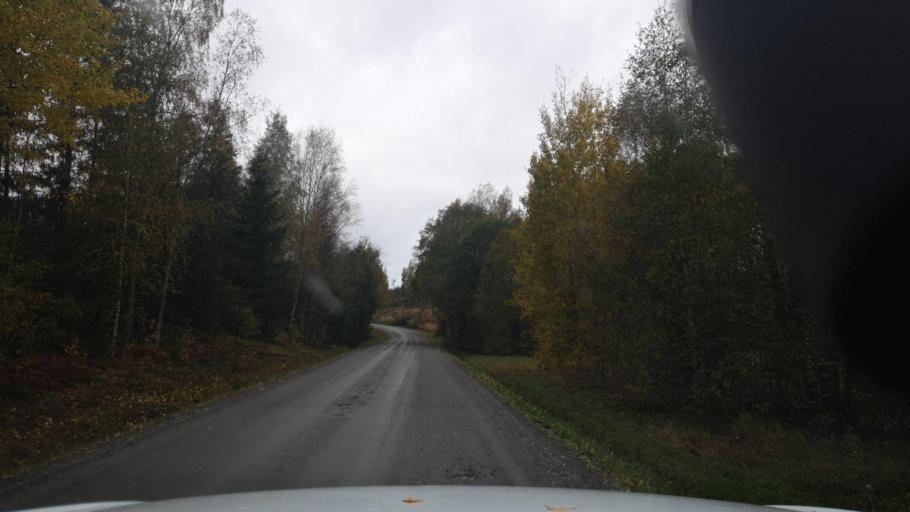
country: SE
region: Vaermland
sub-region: Karlstads Kommun
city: Edsvalla
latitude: 59.4424
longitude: 13.1816
